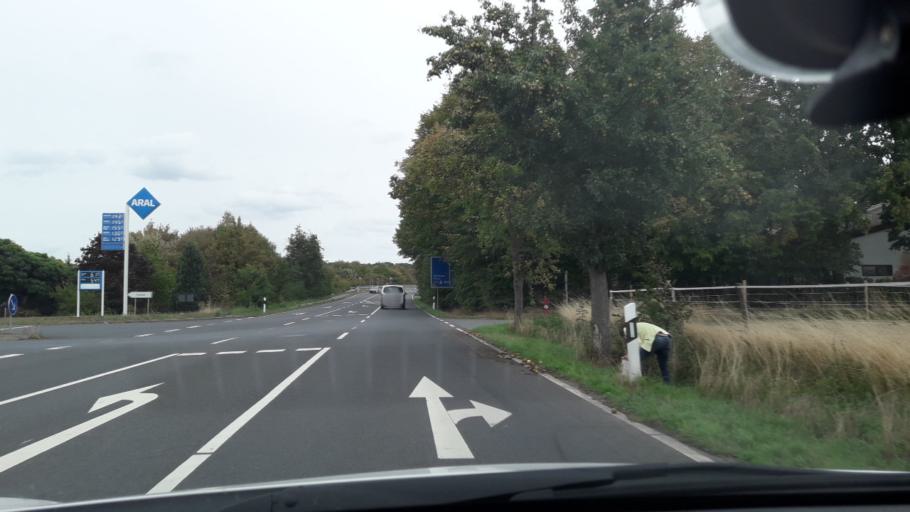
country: DE
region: Lower Saxony
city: Flothe
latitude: 52.0757
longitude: 10.4946
